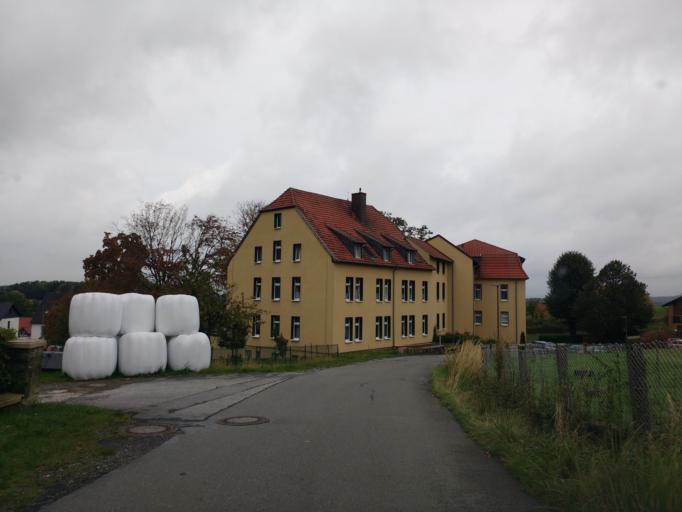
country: DE
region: North Rhine-Westphalia
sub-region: Regierungsbezirk Detmold
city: Horn
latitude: 51.8764
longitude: 8.9092
